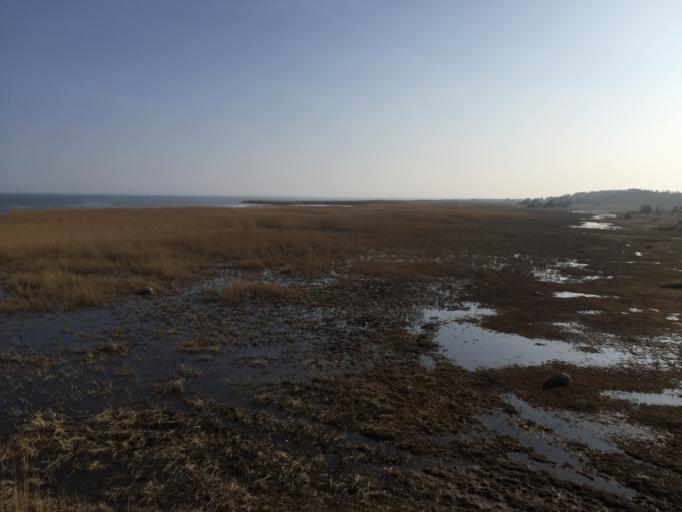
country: EE
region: Saare
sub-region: Kuressaare linn
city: Kuressaare
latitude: 58.2348
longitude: 22.4507
